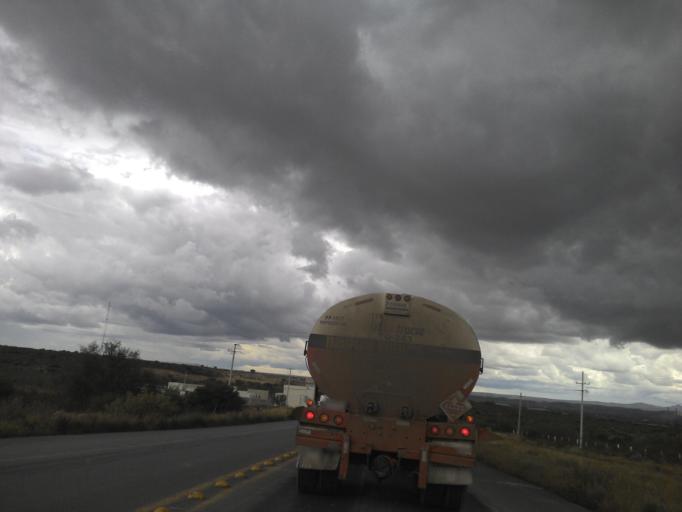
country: MX
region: Zacatecas
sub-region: Rio Grande
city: Los Condes
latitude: 23.8728
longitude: -103.0868
